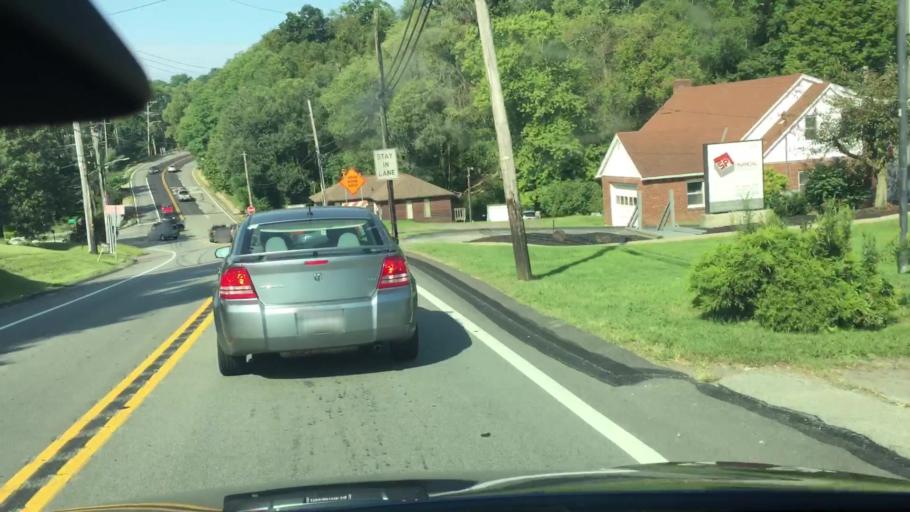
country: US
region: Pennsylvania
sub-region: Allegheny County
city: Monroeville
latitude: 40.4336
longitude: -79.7588
